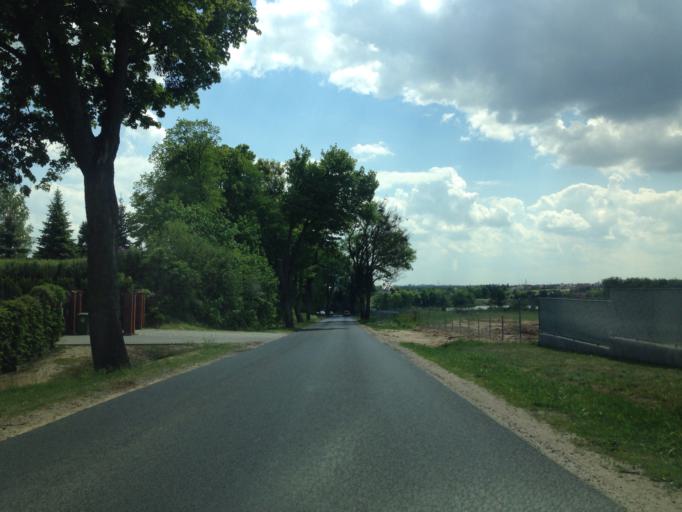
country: PL
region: Kujawsko-Pomorskie
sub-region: Powiat brodnicki
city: Brodnica
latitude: 53.2790
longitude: 19.3869
